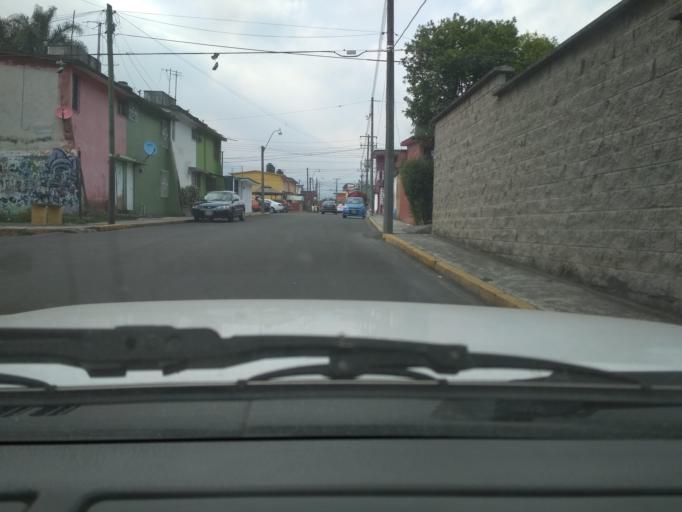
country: MX
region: Veracruz
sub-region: Mariano Escobedo
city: Palmira
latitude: 18.8706
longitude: -97.0988
